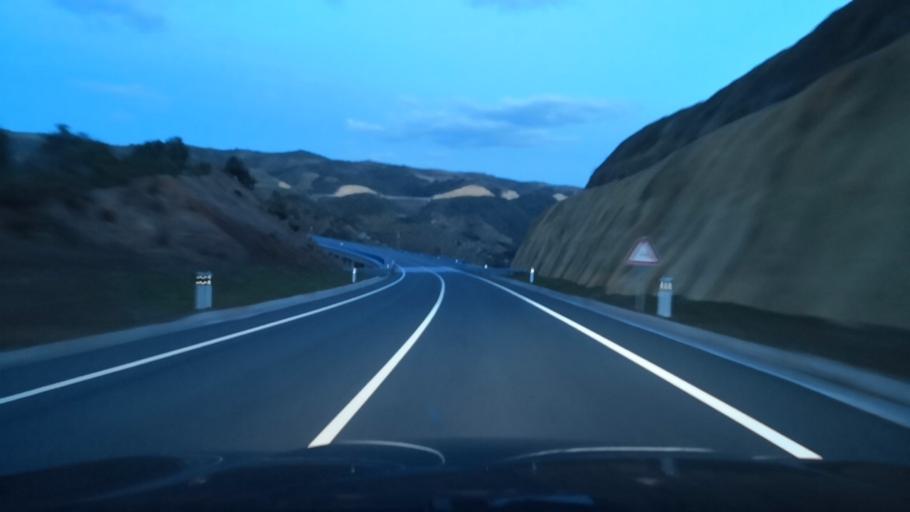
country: PT
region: Braganca
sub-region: Alfandega da Fe
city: Alfandega da Fe
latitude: 41.3088
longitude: -6.9226
